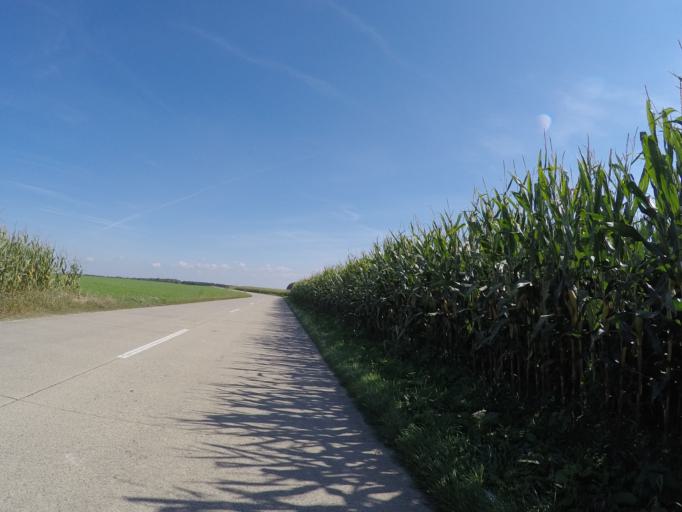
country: BE
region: Wallonia
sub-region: Province de Namur
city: Assesse
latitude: 50.3388
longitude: 4.9942
